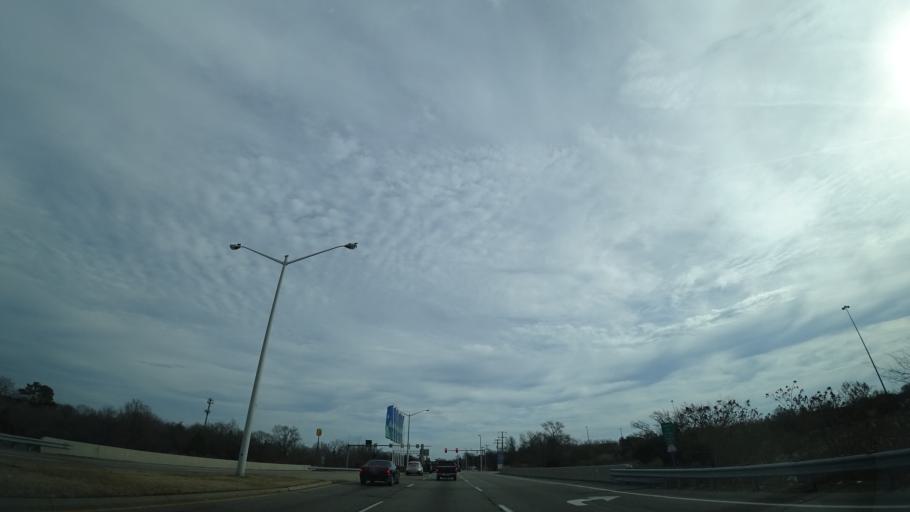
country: US
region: Virginia
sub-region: City of Hampton
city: Hampton
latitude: 37.0355
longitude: -76.3654
